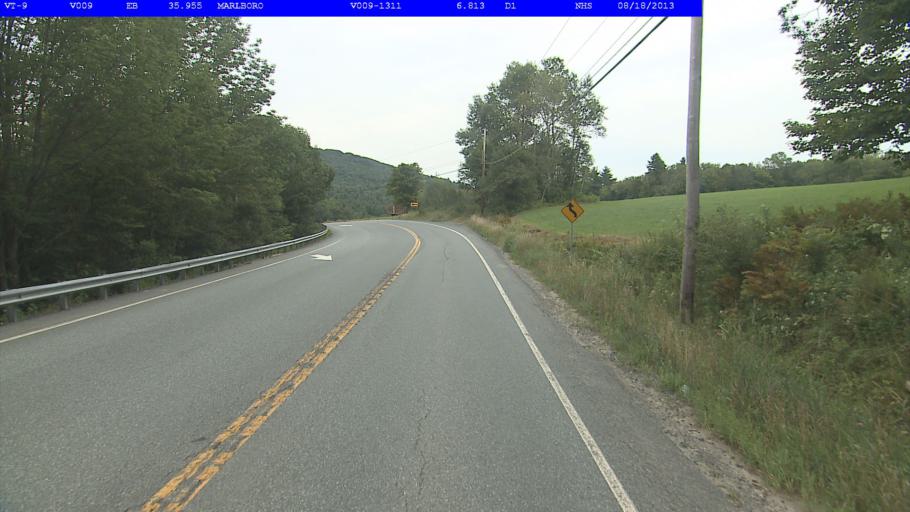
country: US
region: Vermont
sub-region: Windham County
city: West Brattleboro
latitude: 42.8795
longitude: -72.7034
